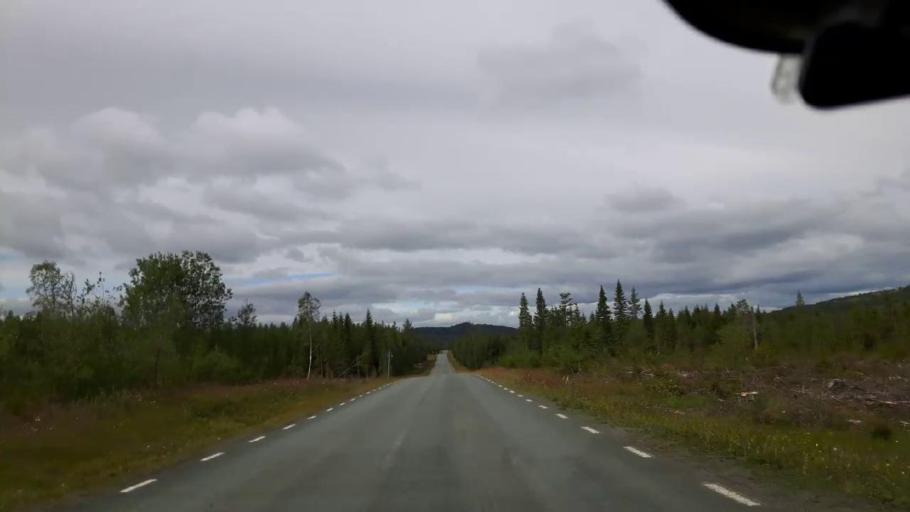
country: SE
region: Jaemtland
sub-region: Krokoms Kommun
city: Valla
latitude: 63.4739
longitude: 14.0026
